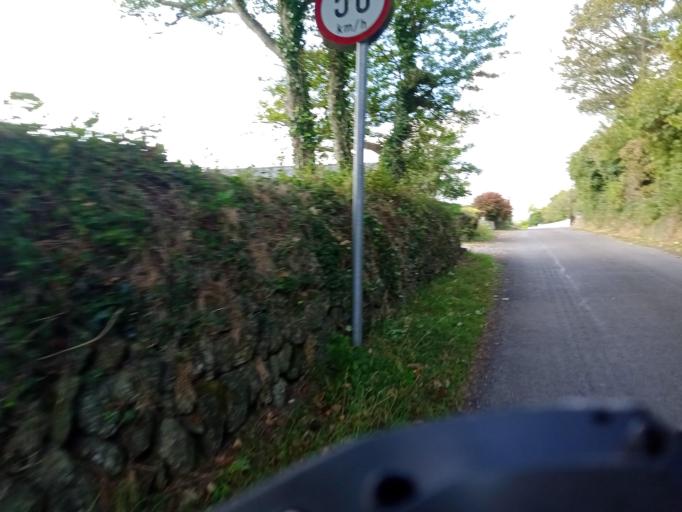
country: IE
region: Munster
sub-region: Waterford
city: Dungarvan
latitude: 52.1280
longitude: -7.4508
